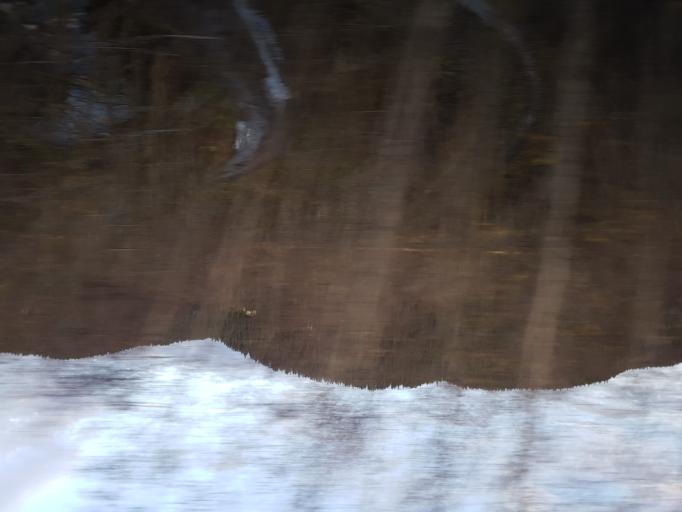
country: NO
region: Sor-Trondelag
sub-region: Melhus
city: Lundamo
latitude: 63.1775
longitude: 10.3109
